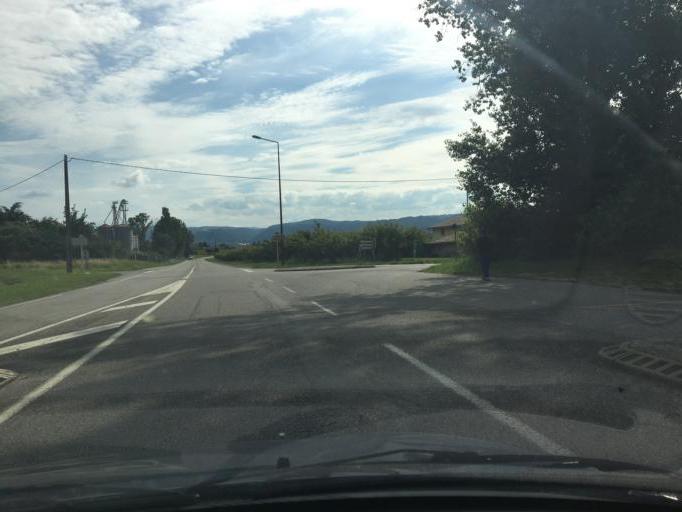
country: FR
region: Rhone-Alpes
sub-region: Departement de la Drome
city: Mercurol
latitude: 45.0729
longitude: 4.8838
